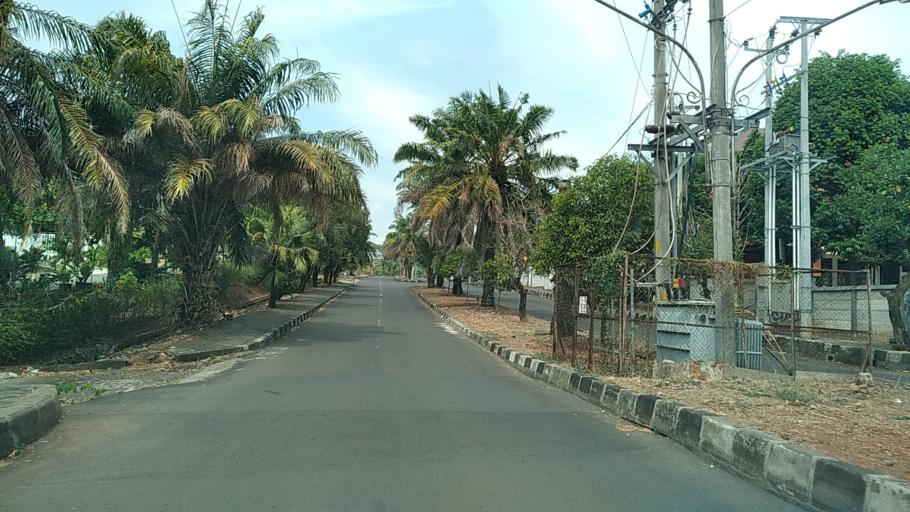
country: ID
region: Central Java
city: Semarang
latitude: -7.0466
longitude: 110.4403
